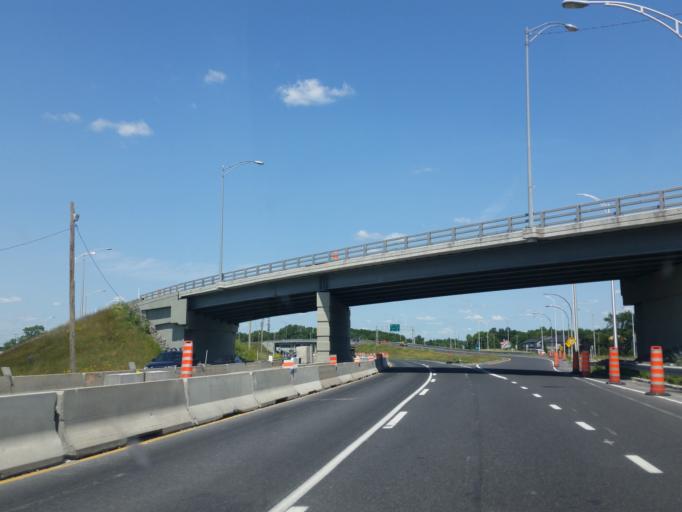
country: CA
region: Quebec
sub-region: Monteregie
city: Saint-Jean-sur-Richelieu
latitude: 45.3450
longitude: -73.2876
